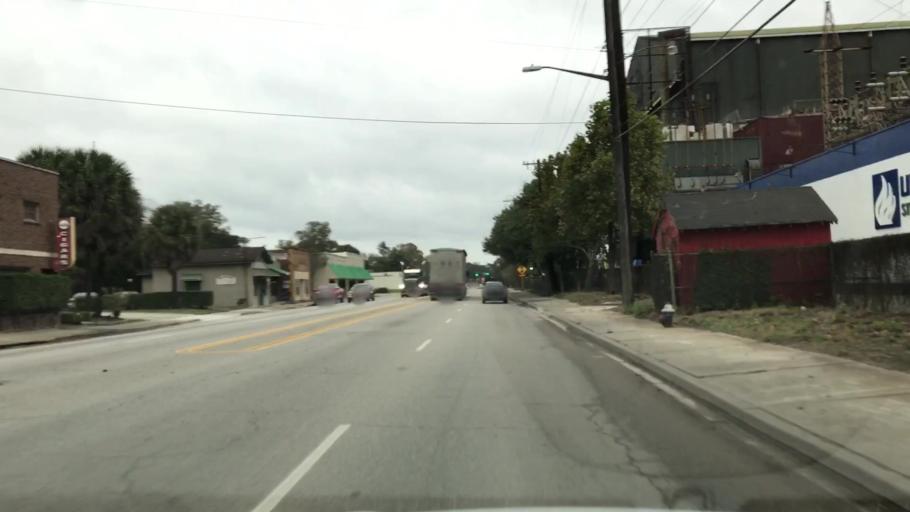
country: US
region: South Carolina
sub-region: Georgetown County
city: Georgetown
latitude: 33.3688
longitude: -79.2923
